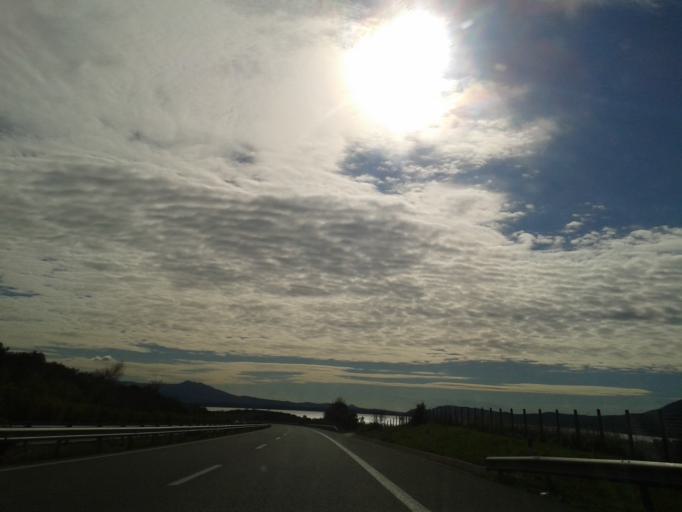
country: GR
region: West Greece
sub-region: Nomos Aitolias kai Akarnanias
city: Fitiai
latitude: 38.6851
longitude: 21.2175
